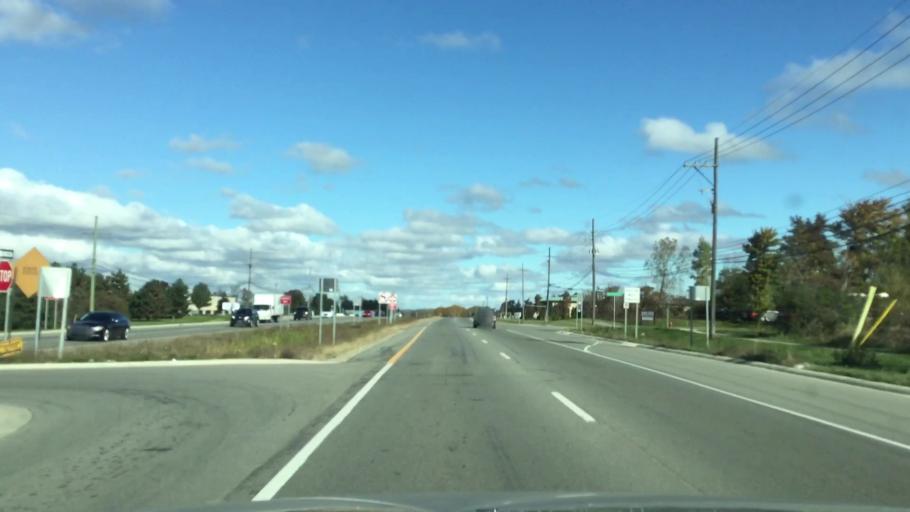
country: US
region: Michigan
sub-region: Oakland County
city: Auburn Hills
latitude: 42.7158
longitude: -83.2425
